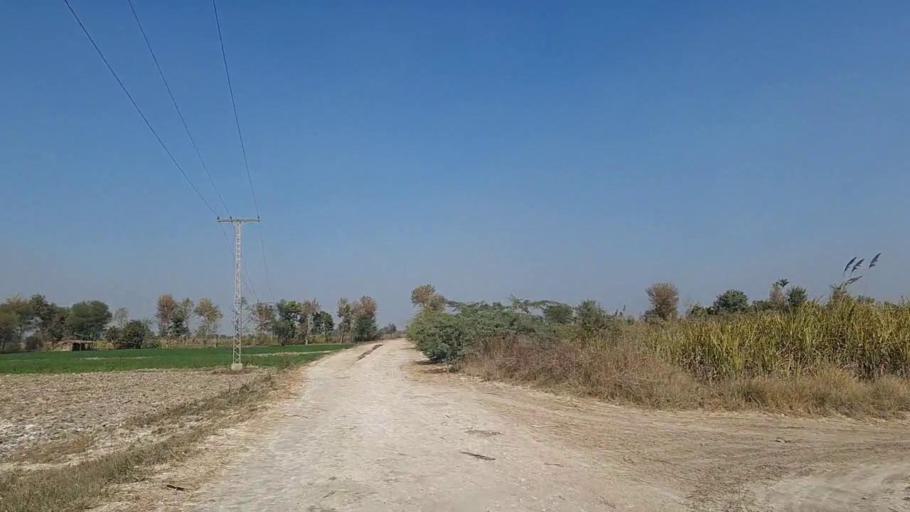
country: PK
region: Sindh
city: Daur
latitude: 26.4876
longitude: 68.3384
